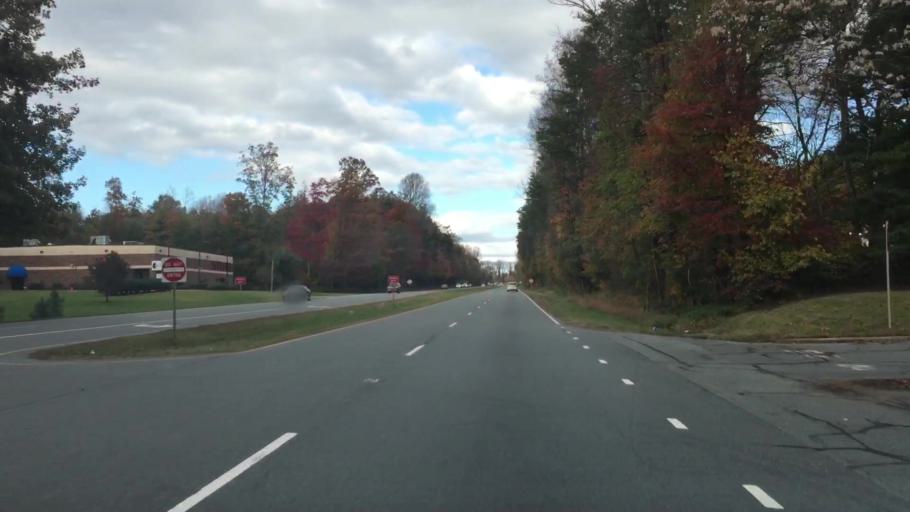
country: US
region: North Carolina
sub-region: Forsyth County
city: Winston-Salem
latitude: 36.1074
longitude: -80.1909
